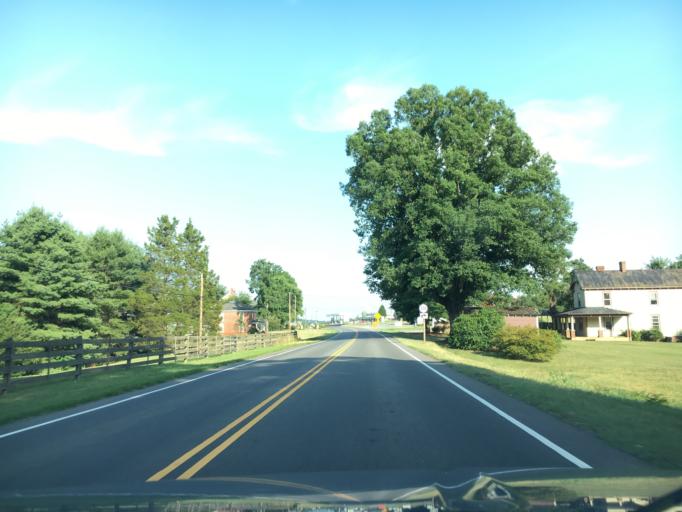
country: US
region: Virginia
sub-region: Franklin County
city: Union Hall
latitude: 36.9909
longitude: -79.7660
